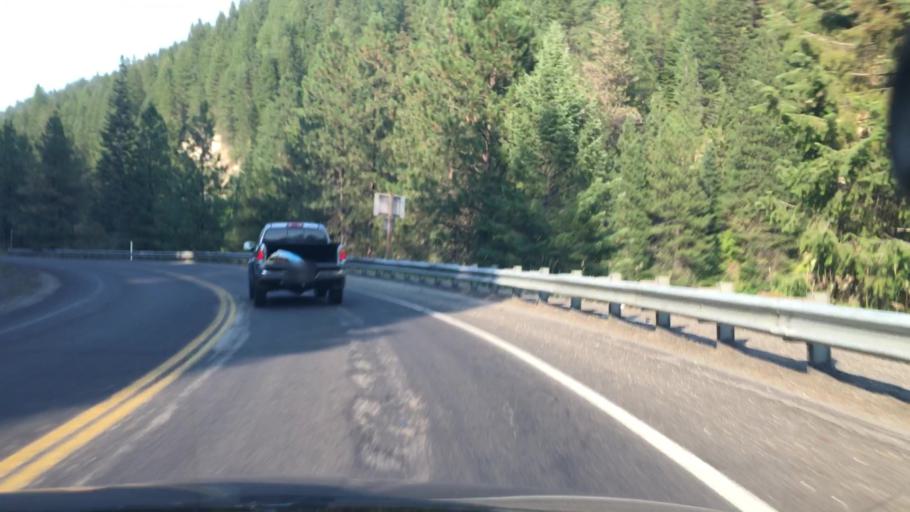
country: US
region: Idaho
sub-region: Valley County
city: Cascade
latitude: 44.2508
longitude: -116.0883
